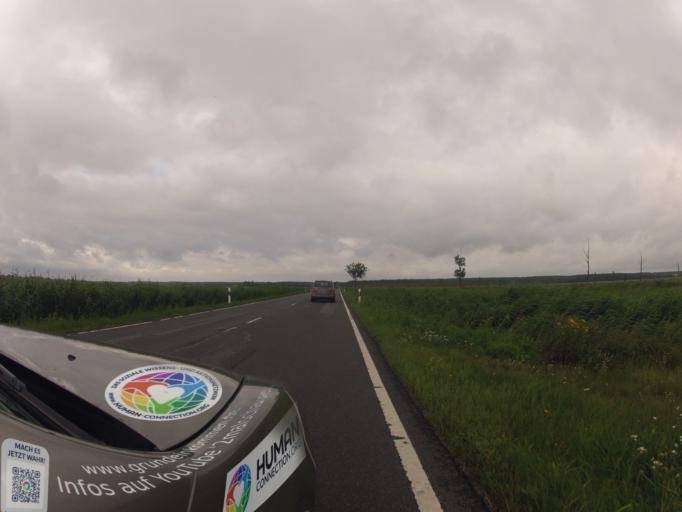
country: DE
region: Mecklenburg-Vorpommern
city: Lassan
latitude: 53.8688
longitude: 13.8159
